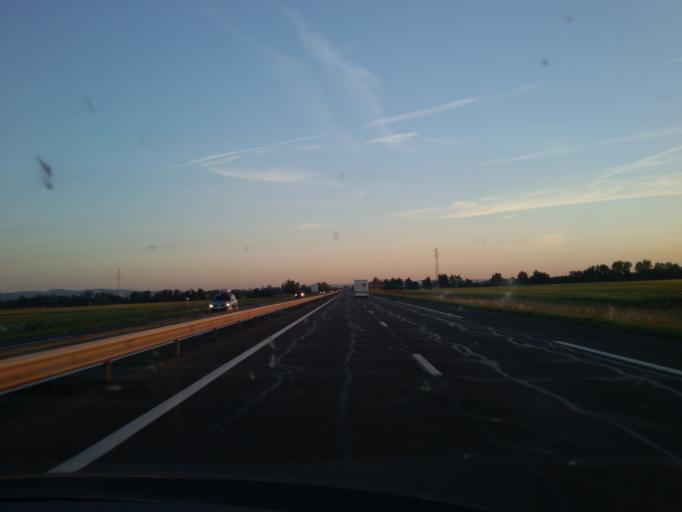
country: FR
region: Auvergne
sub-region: Departement du Puy-de-Dome
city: Menetrol
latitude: 45.8595
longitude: 3.1589
